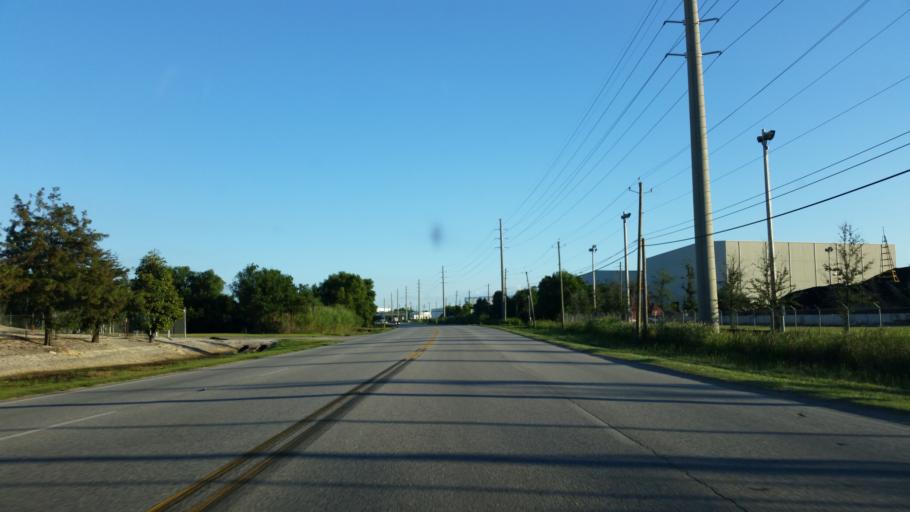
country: US
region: Alabama
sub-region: Mobile County
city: Mobile
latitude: 30.7037
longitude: -88.0330
